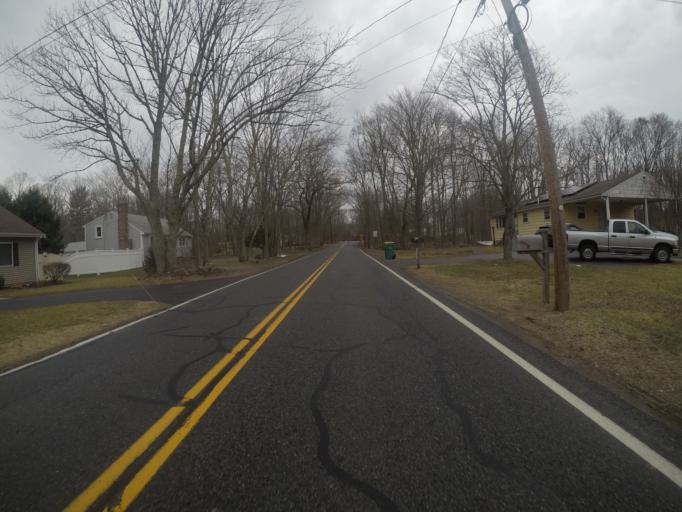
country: US
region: Massachusetts
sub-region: Bristol County
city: Easton
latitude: 42.0479
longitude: -71.1593
